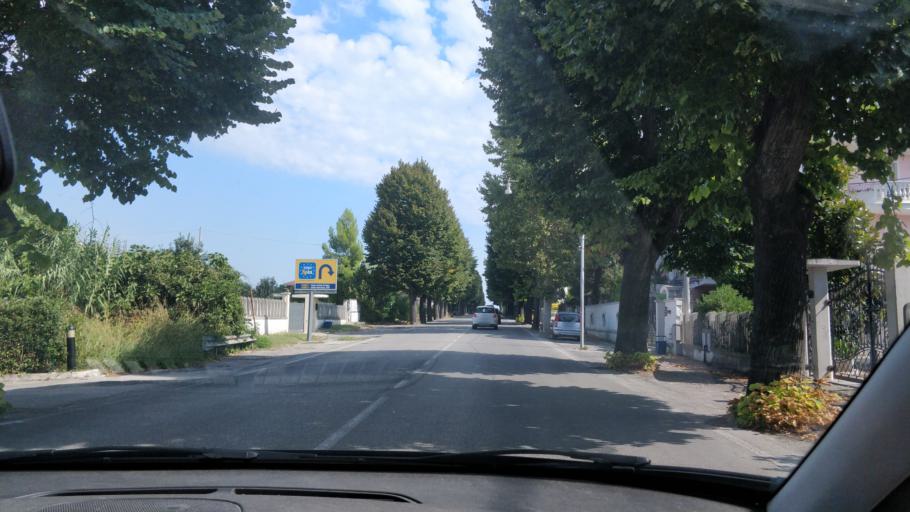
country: IT
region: Abruzzo
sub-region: Provincia di Chieti
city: Chieti
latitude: 42.3911
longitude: 14.1596
